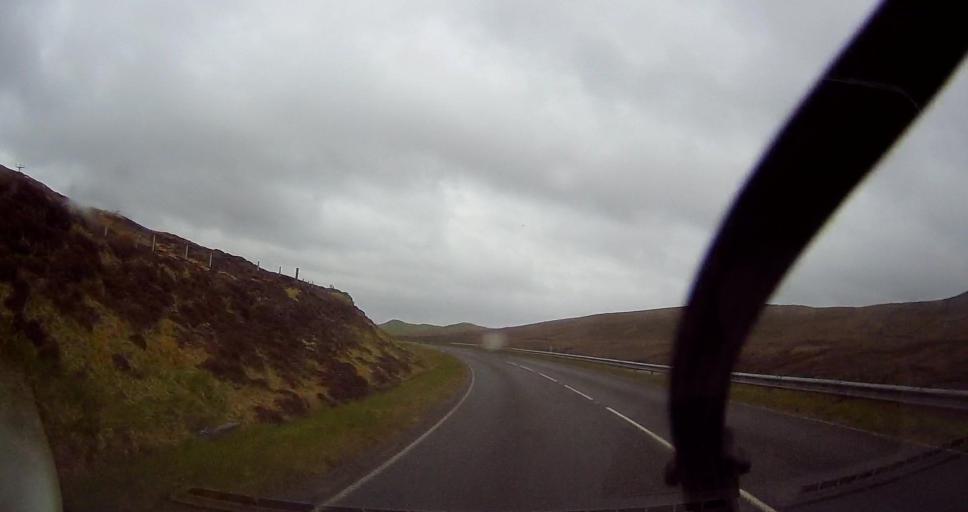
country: GB
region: Scotland
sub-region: Shetland Islands
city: Lerwick
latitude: 60.4406
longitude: -1.3973
